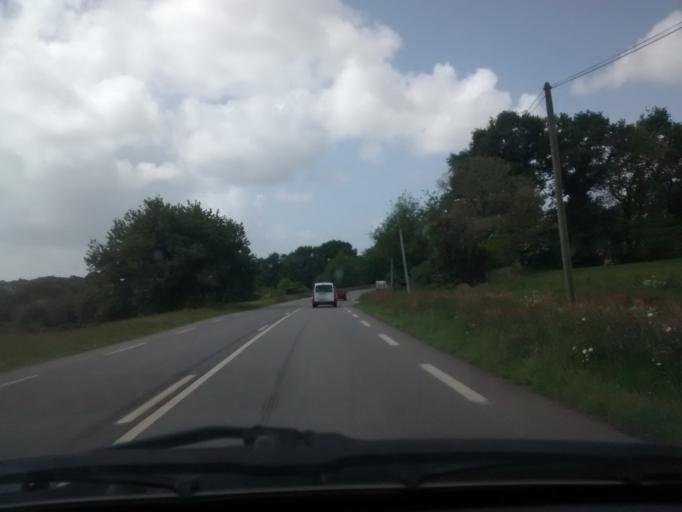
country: FR
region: Brittany
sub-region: Departement du Morbihan
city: Arradon
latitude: 47.6329
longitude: -2.8419
